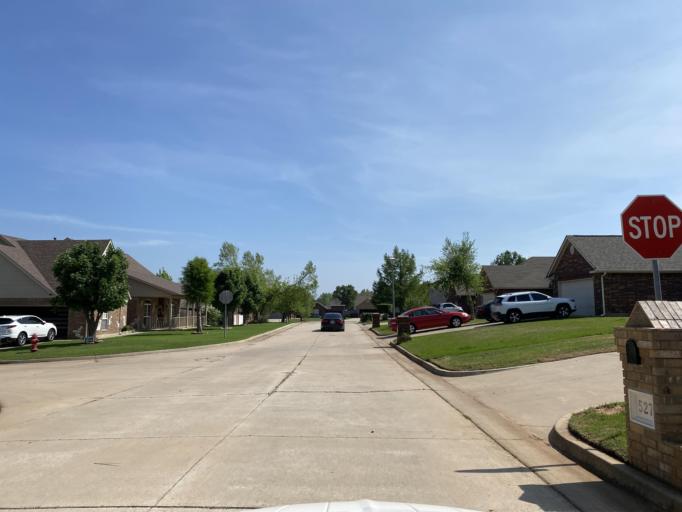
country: US
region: Oklahoma
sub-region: Oklahoma County
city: Nicoma Park
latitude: 35.4726
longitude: -97.3397
